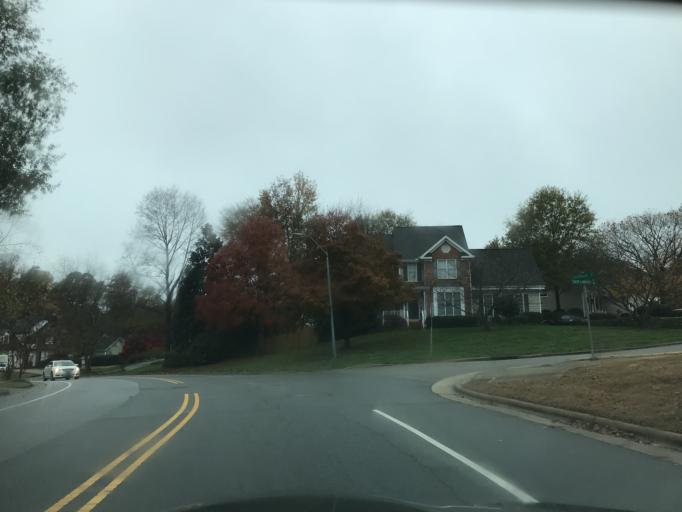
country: US
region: North Carolina
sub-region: Wake County
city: West Raleigh
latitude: 35.8357
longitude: -78.6283
